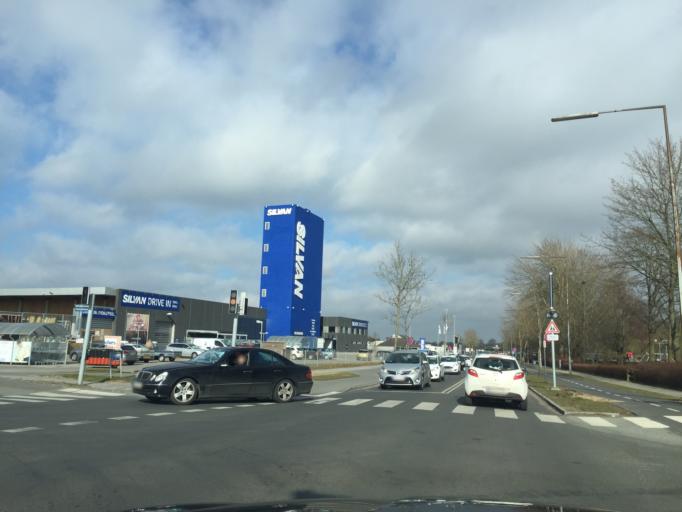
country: DK
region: South Denmark
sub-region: Odense Kommune
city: Neder Holluf
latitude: 55.3791
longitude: 10.4228
